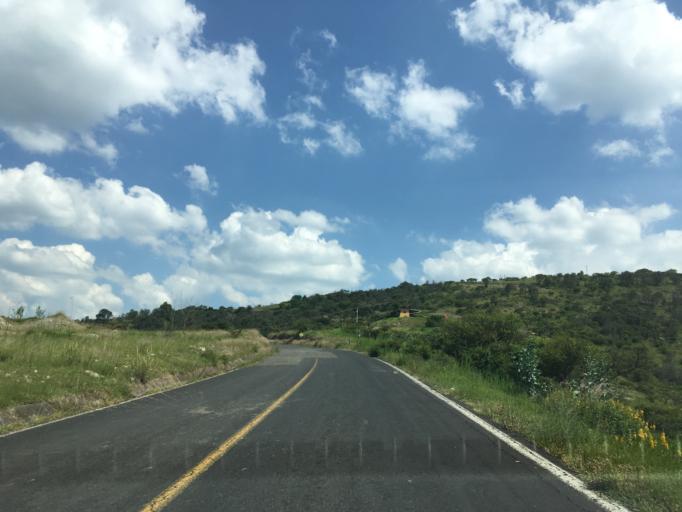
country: MX
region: Michoacan
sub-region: Morelia
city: Morelos
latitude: 19.6437
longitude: -101.2033
